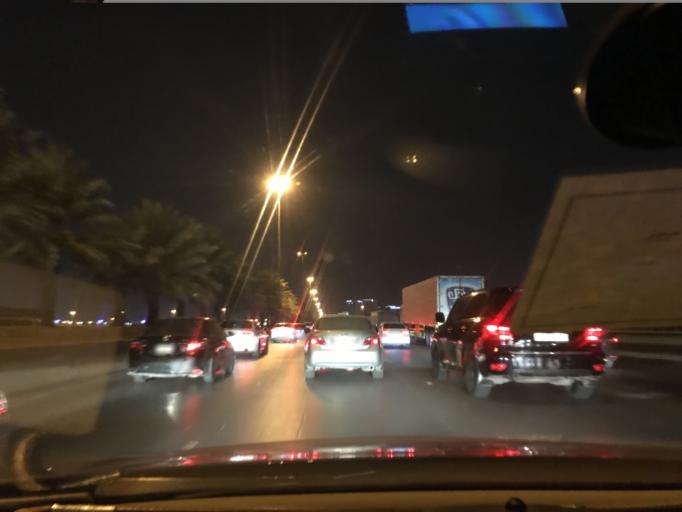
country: SA
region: Ar Riyad
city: Riyadh
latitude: 24.7693
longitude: 46.7342
